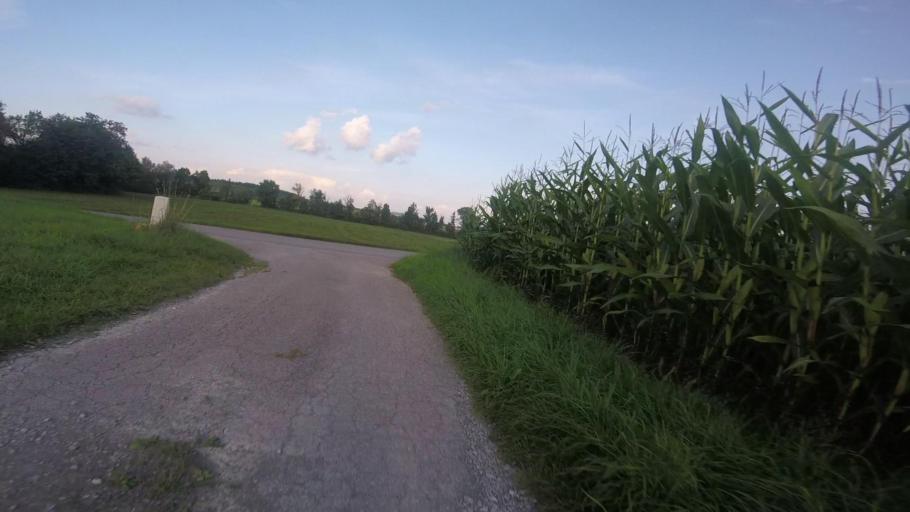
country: DE
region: Baden-Wuerttemberg
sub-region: Regierungsbezirk Stuttgart
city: Aspach
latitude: 48.9725
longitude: 9.3743
